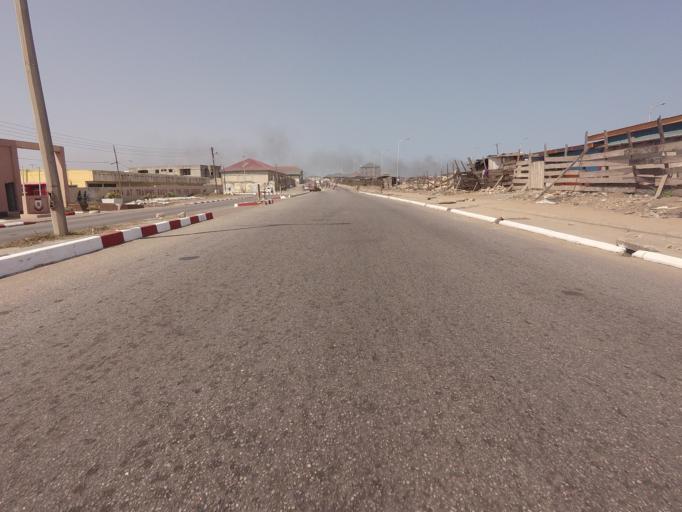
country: GH
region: Greater Accra
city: Accra
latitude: 5.5320
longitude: -0.2169
